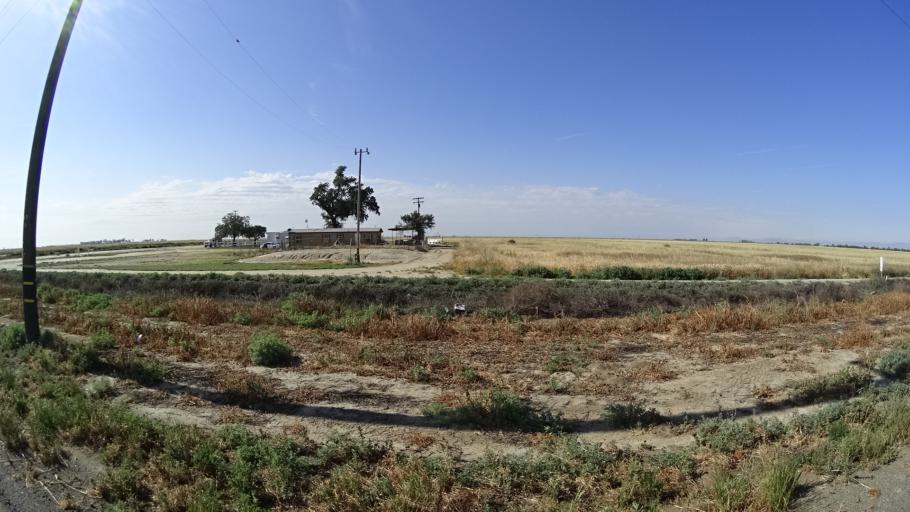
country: US
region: California
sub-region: Kings County
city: Armona
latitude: 36.2256
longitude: -119.7275
